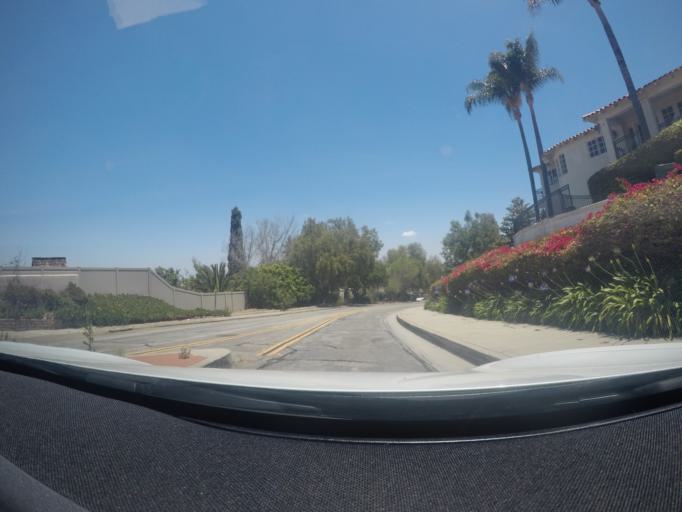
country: US
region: California
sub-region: Los Angeles County
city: Rolling Hills Estates
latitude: 33.7985
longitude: -118.3534
